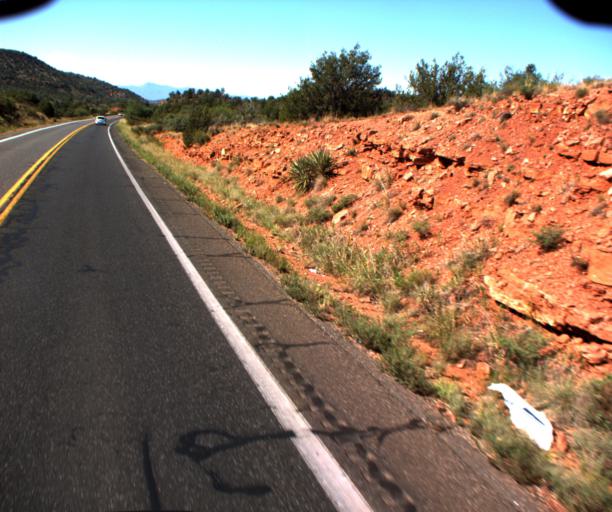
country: US
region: Arizona
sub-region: Yavapai County
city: Big Park
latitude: 34.7502
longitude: -111.7658
